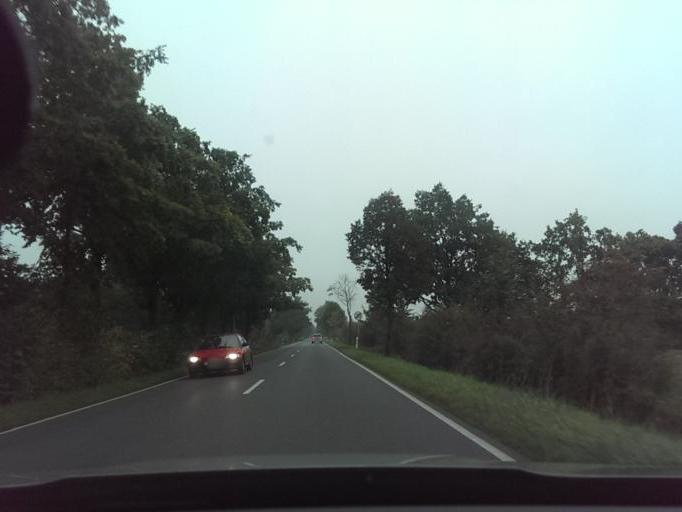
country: DE
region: Lower Saxony
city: Garbsen-Mitte
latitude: 52.4578
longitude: 9.6478
